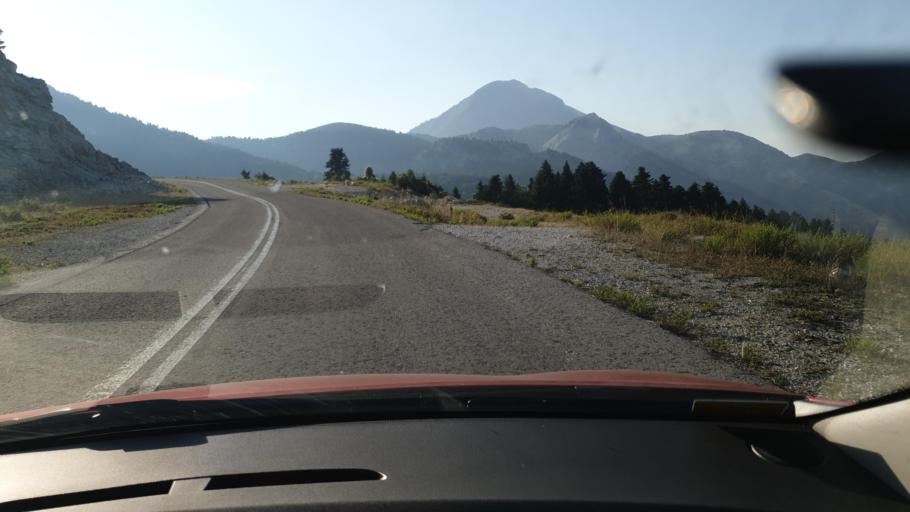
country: GR
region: Central Greece
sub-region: Nomos Evvoias
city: Yimnon
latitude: 38.5940
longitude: 23.8906
